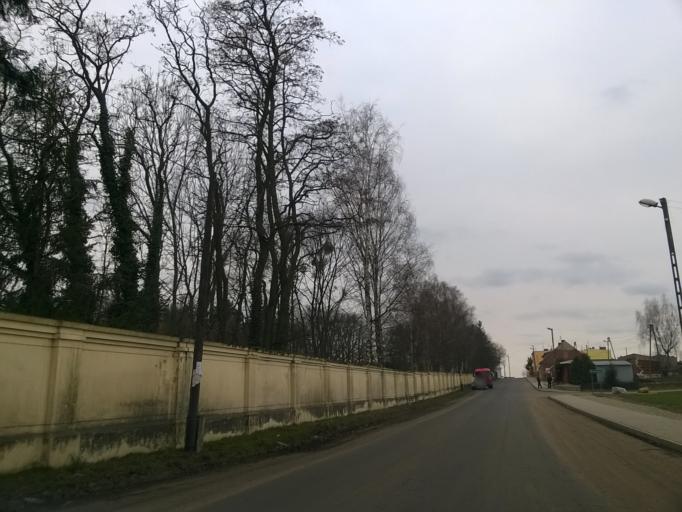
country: PL
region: Greater Poland Voivodeship
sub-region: Powiat poznanski
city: Murowana Goslina
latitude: 52.6196
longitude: 17.0503
